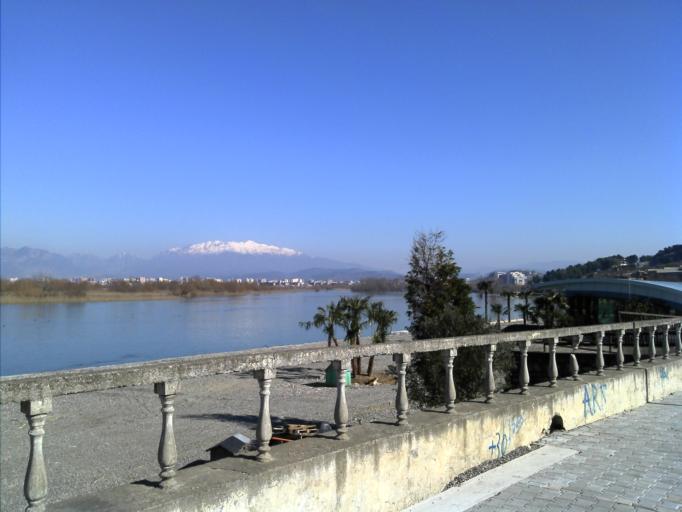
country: AL
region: Shkoder
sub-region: Rrethi i Shkodres
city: Shkoder
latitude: 42.0545
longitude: 19.4770
